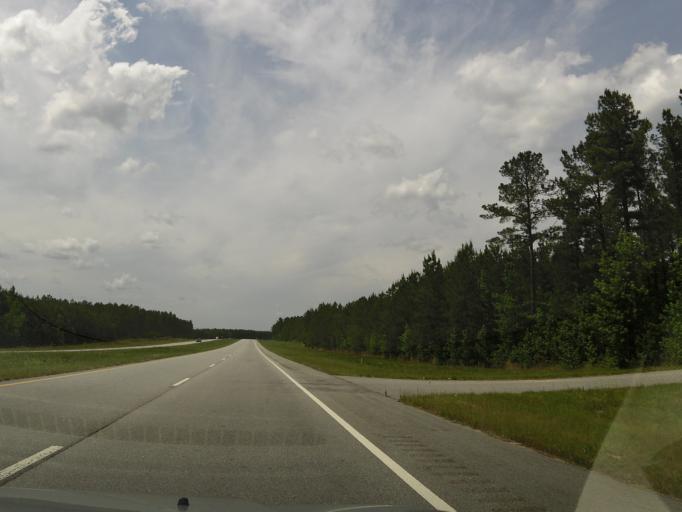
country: US
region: Georgia
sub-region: Jefferson County
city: Wadley
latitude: 32.7807
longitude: -82.3895
